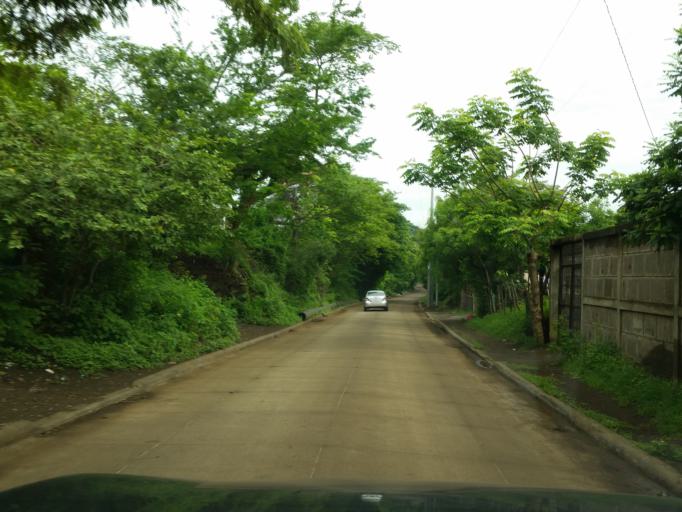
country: NI
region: Managua
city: Managua
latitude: 12.0998
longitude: -86.2154
